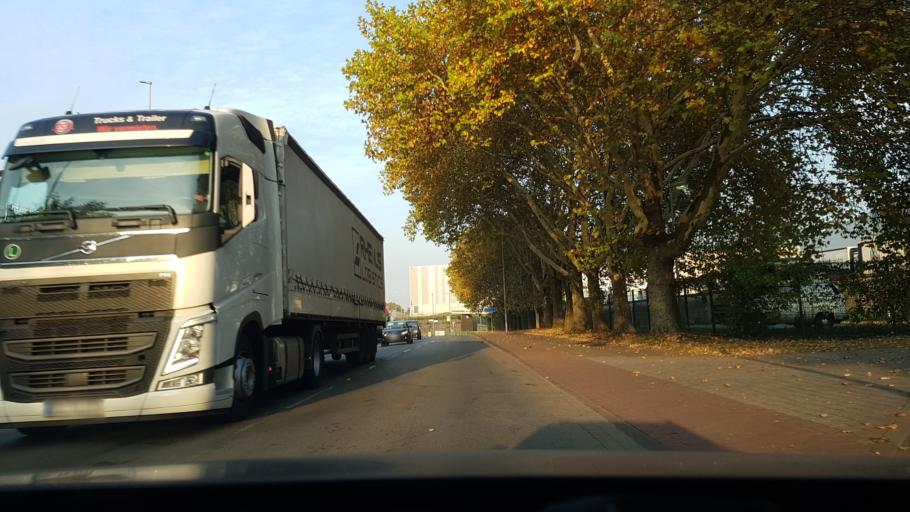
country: DE
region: North Rhine-Westphalia
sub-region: Regierungsbezirk Dusseldorf
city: Hochfeld
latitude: 51.4007
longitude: 6.7224
